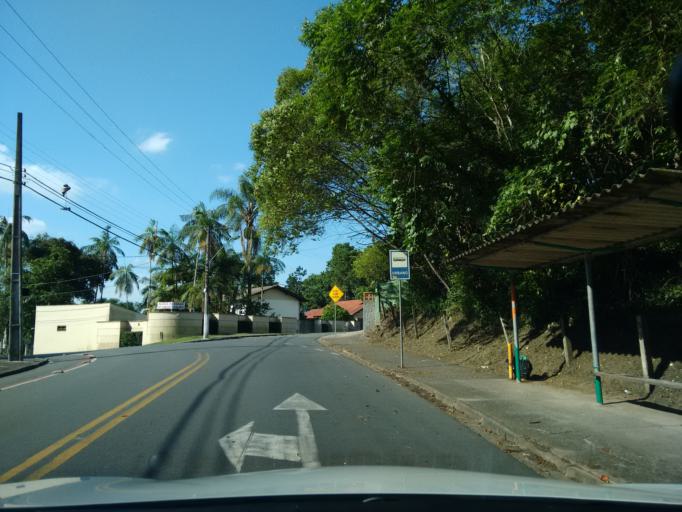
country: BR
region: Santa Catarina
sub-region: Blumenau
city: Blumenau
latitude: -26.8978
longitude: -49.0654
